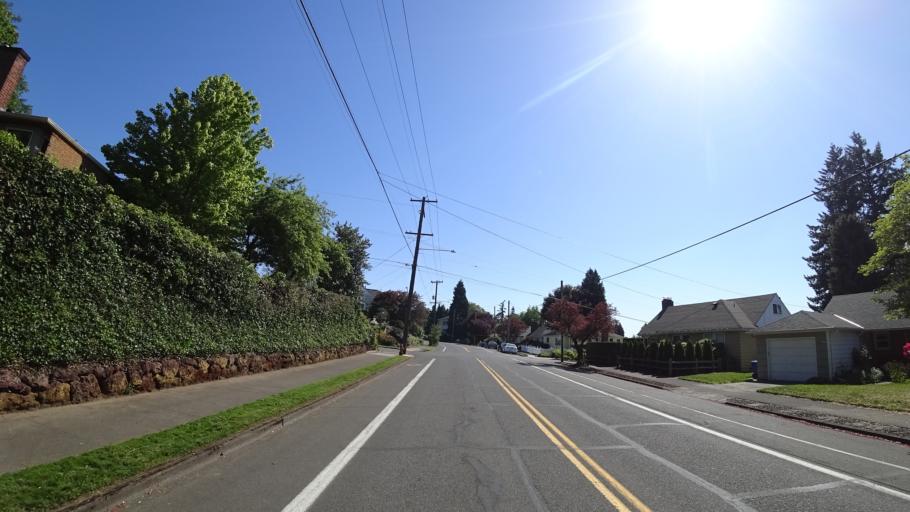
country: US
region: Oregon
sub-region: Clackamas County
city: Milwaukie
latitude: 45.4884
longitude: -122.6202
